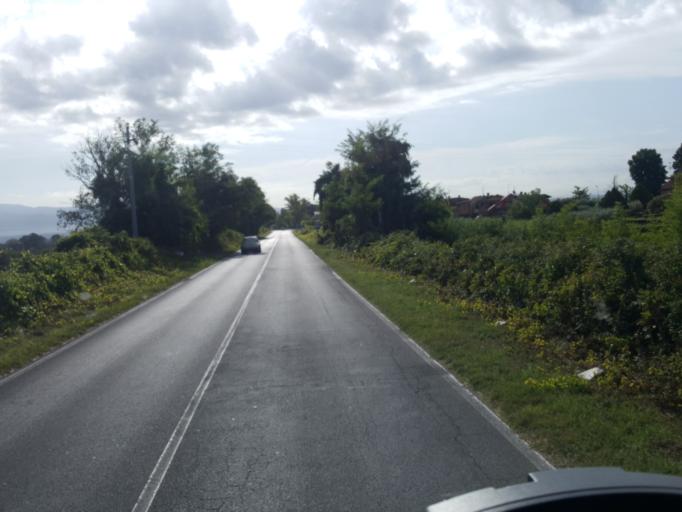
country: IT
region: Latium
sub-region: Citta metropolitana di Roma Capitale
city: Capena
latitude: 42.1334
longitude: 12.5574
